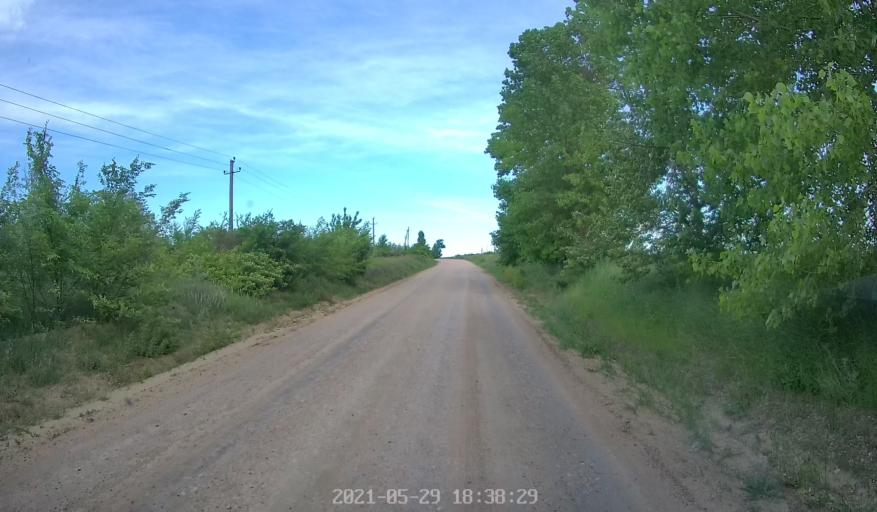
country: MD
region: Chisinau
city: Singera
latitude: 46.8020
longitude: 28.9379
